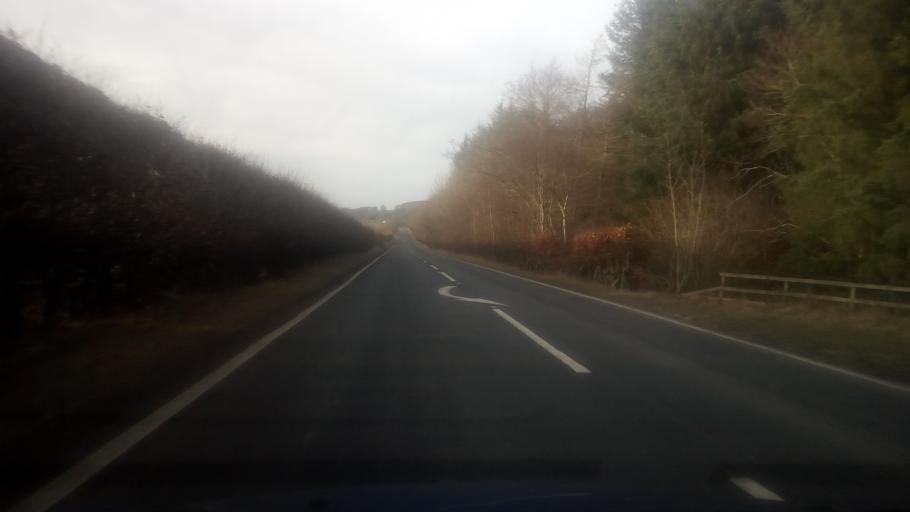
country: GB
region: Scotland
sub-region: The Scottish Borders
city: Jedburgh
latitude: 55.4239
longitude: -2.5293
